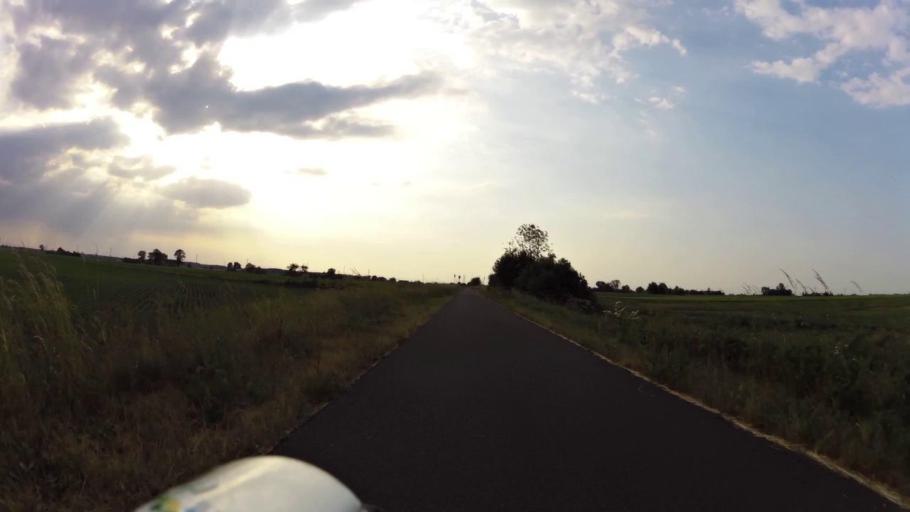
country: PL
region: Kujawsko-Pomorskie
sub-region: Powiat chelminski
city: Unislaw
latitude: 53.1738
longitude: 18.4175
